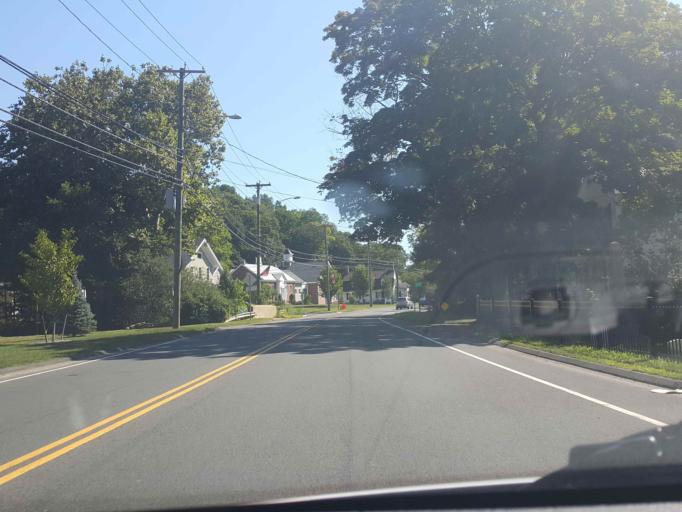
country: US
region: Connecticut
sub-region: New Haven County
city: North Branford
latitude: 41.3282
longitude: -72.7668
